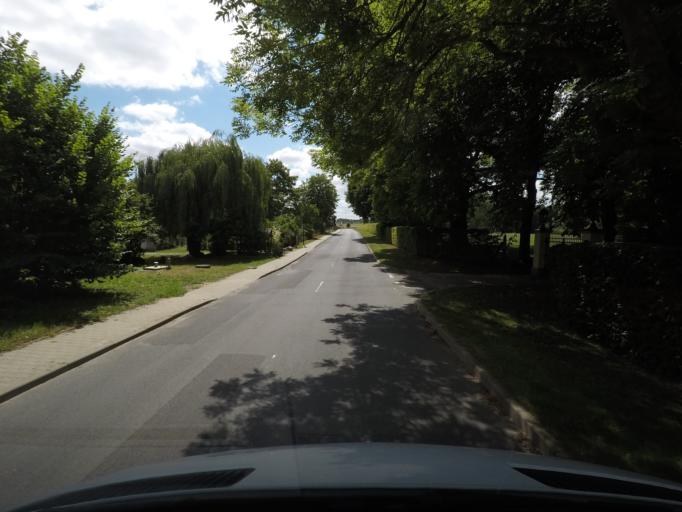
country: DE
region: Brandenburg
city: Brussow
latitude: 53.3206
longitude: 14.1198
